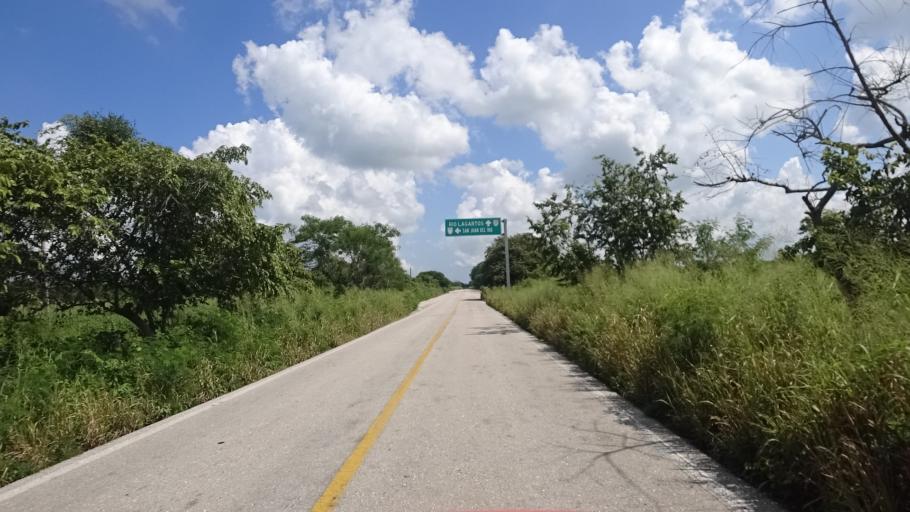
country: MX
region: Yucatan
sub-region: Panaba
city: Loche
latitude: 21.4446
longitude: -88.1384
